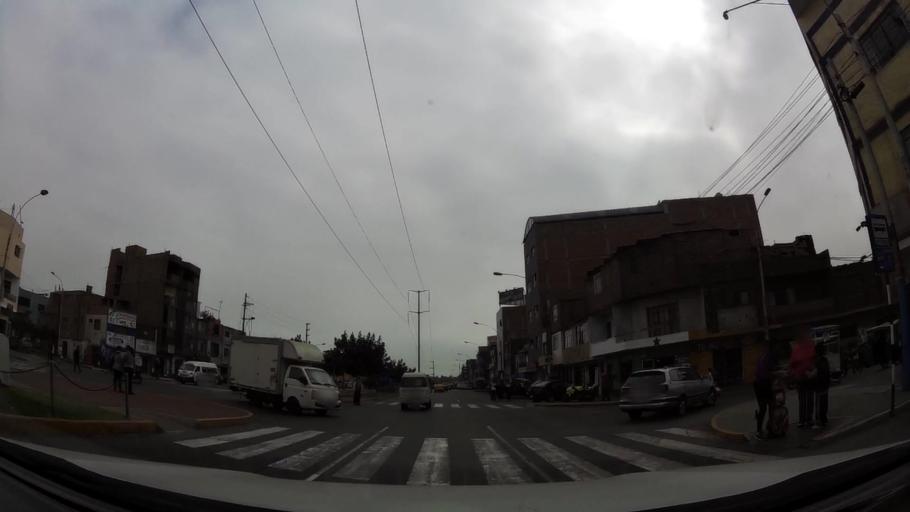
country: PE
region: Callao
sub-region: Callao
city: Callao
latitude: -12.0302
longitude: -77.0913
